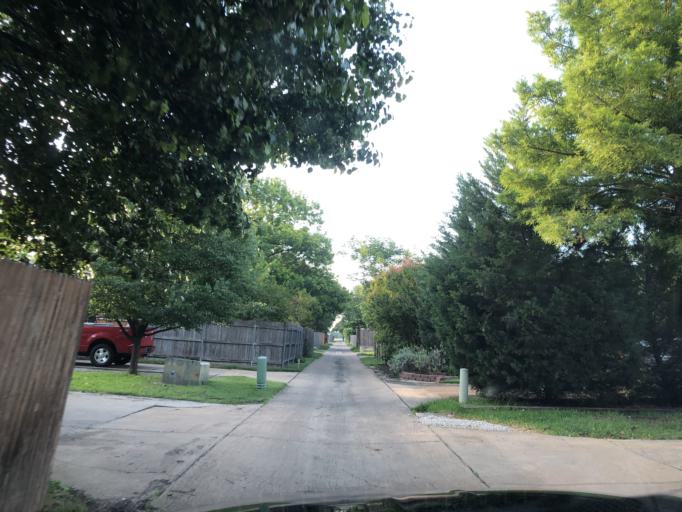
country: US
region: Texas
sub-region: Dallas County
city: Garland
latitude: 32.8461
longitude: -96.6229
